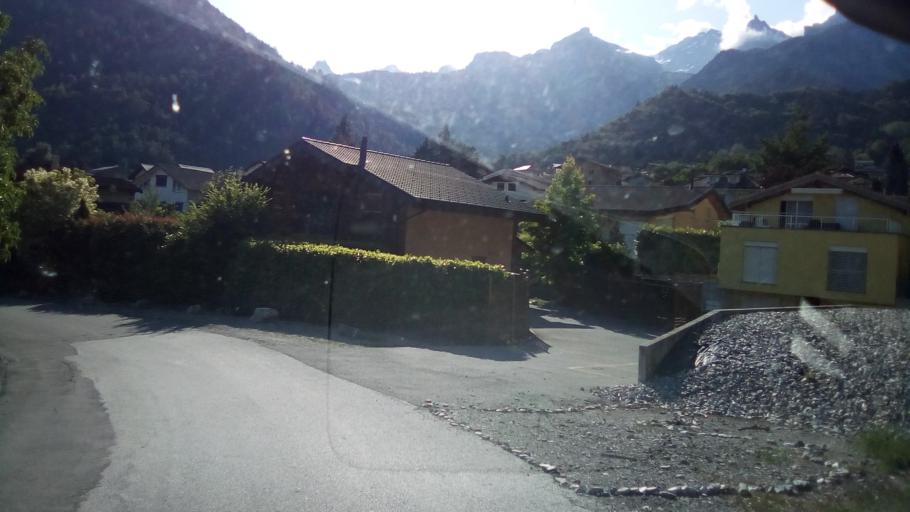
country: CH
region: Valais
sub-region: Conthey District
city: Chamoson
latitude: 46.2060
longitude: 7.2238
